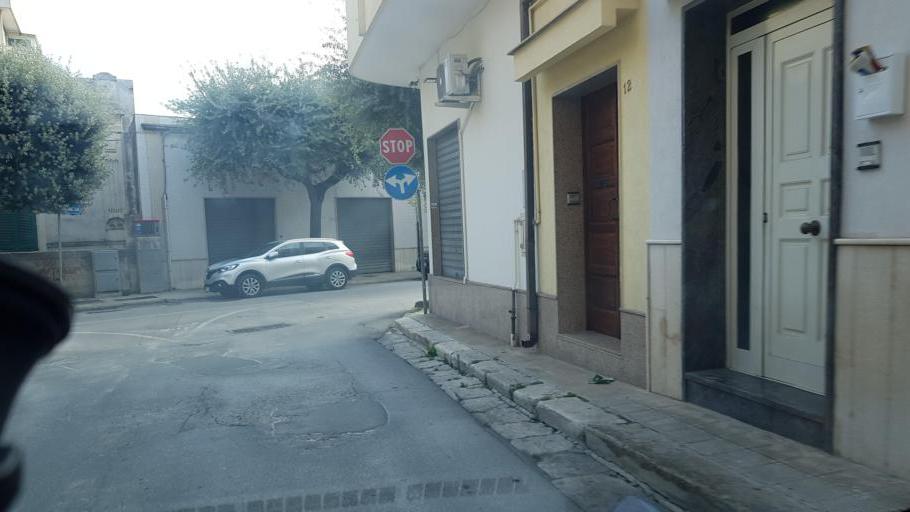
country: IT
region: Apulia
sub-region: Provincia di Brindisi
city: Francavilla Fontana
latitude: 40.5255
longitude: 17.5870
